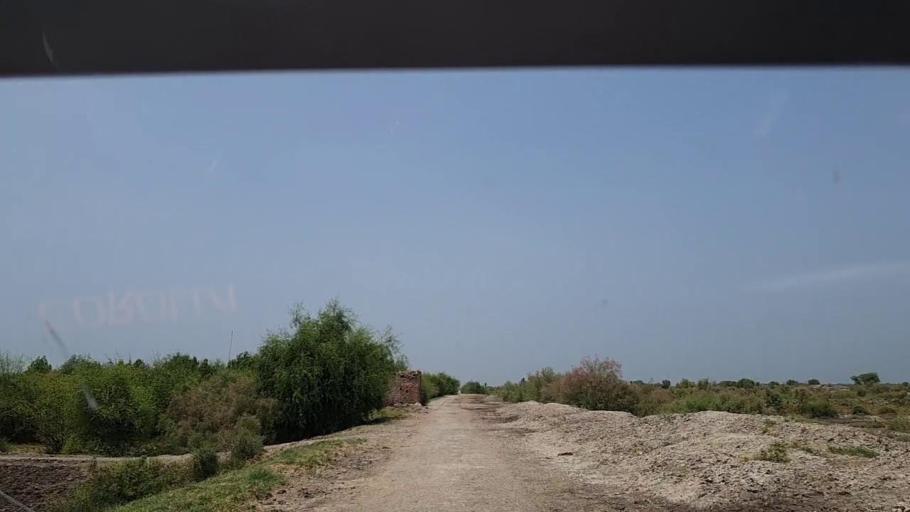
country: PK
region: Sindh
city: Adilpur
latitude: 27.8914
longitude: 69.2494
